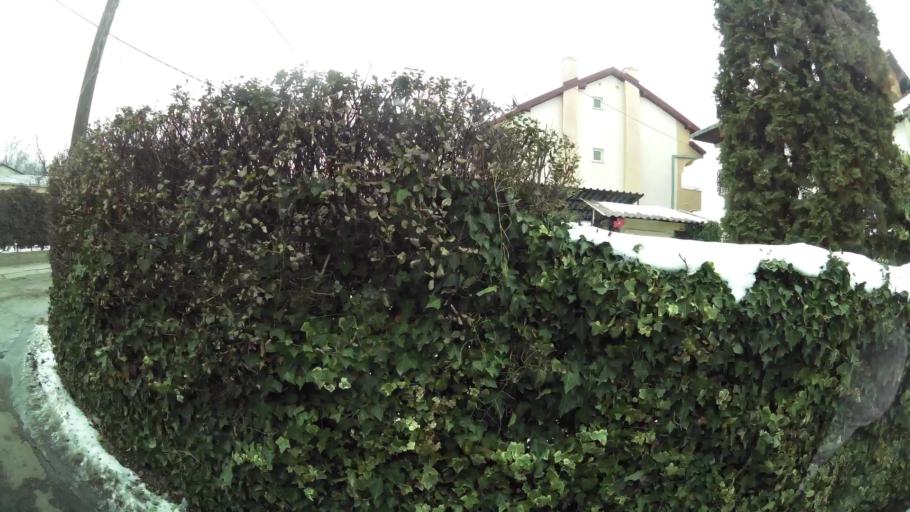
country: MK
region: Butel
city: Butel
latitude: 42.0365
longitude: 21.4454
